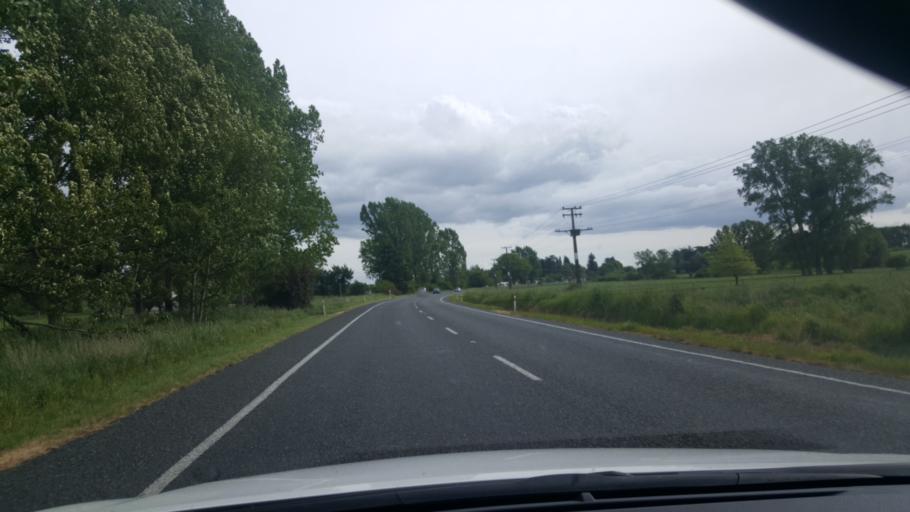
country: NZ
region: Waikato
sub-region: Taupo District
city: Taupo
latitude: -38.4628
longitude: 176.3149
